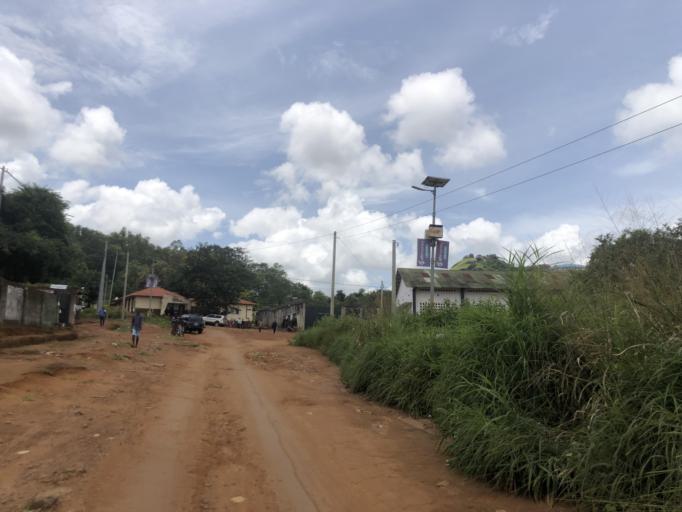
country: SL
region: Northern Province
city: Makeni
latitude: 8.8774
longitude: -12.0534
